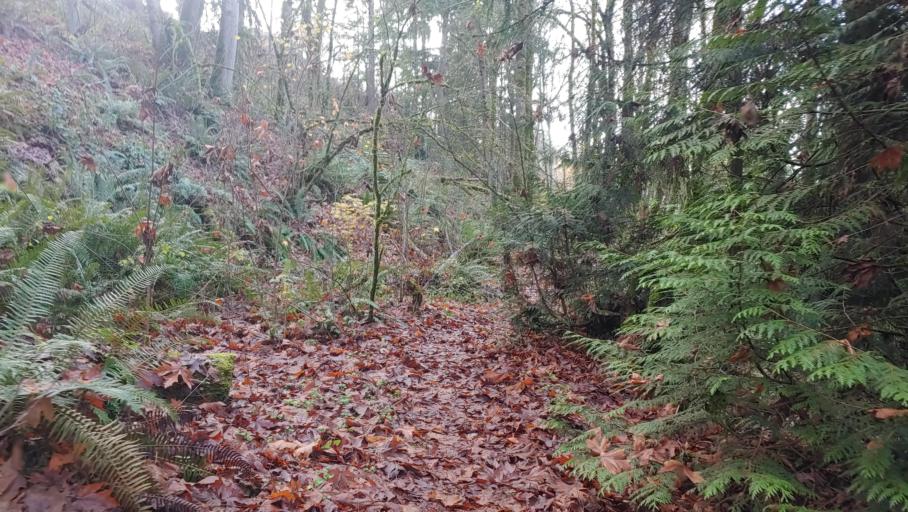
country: US
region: Washington
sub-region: King County
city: Eastgate
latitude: 47.5694
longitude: -122.1509
